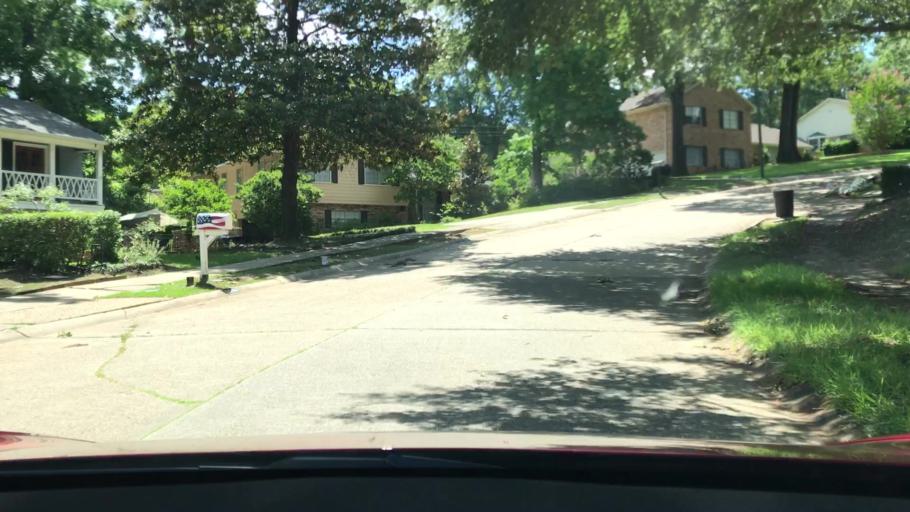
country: US
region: Louisiana
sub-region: Bossier Parish
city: Bossier City
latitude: 32.4277
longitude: -93.7289
